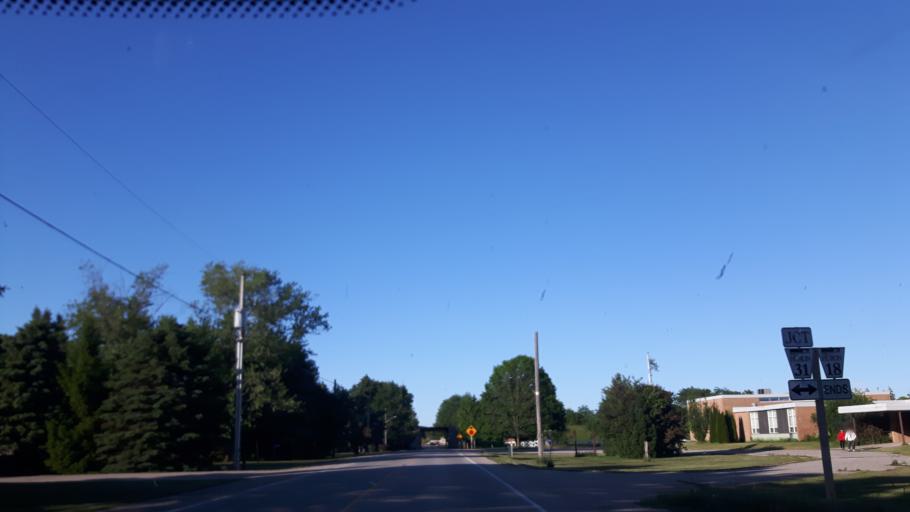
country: CA
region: Ontario
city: Goderich
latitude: 43.6437
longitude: -81.6060
